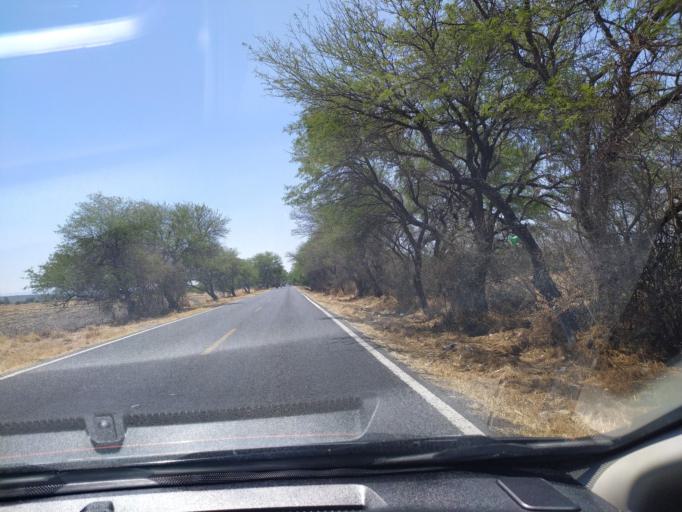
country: MX
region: Guanajuato
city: San Roque
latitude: 20.9629
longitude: -101.8470
